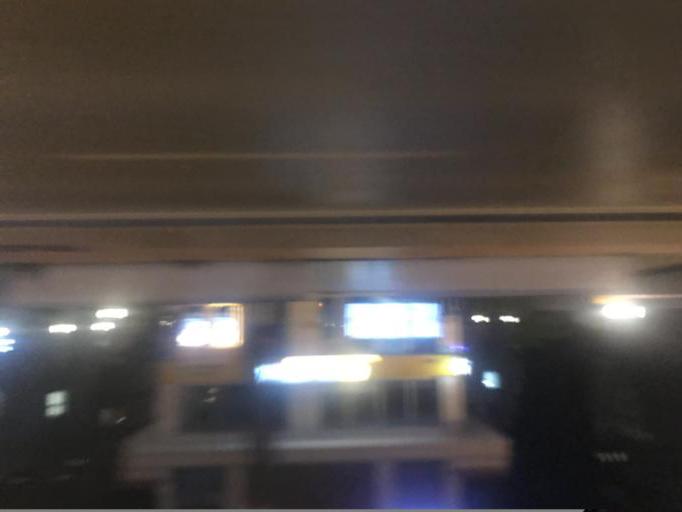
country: TR
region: Istanbul
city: Bahcelievler
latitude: 40.9869
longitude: 28.8722
